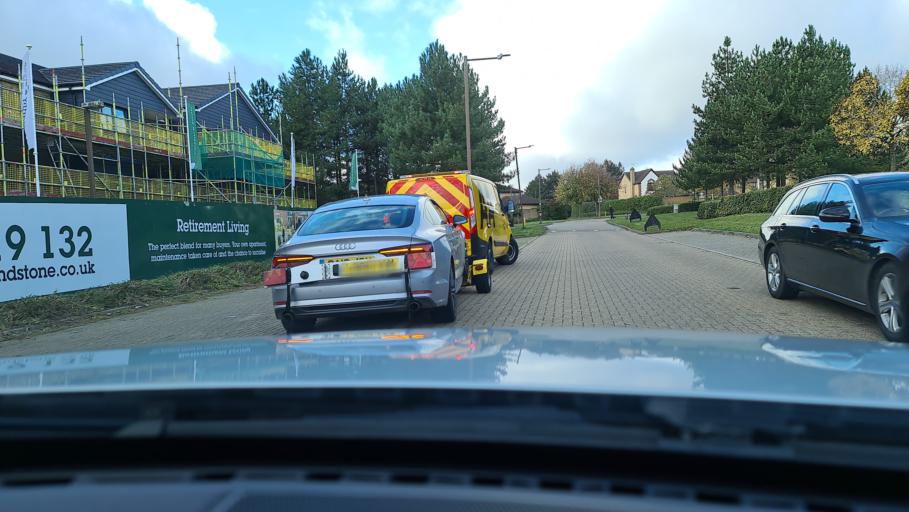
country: GB
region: England
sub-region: Milton Keynes
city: Simpson
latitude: 52.0211
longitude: -0.6917
